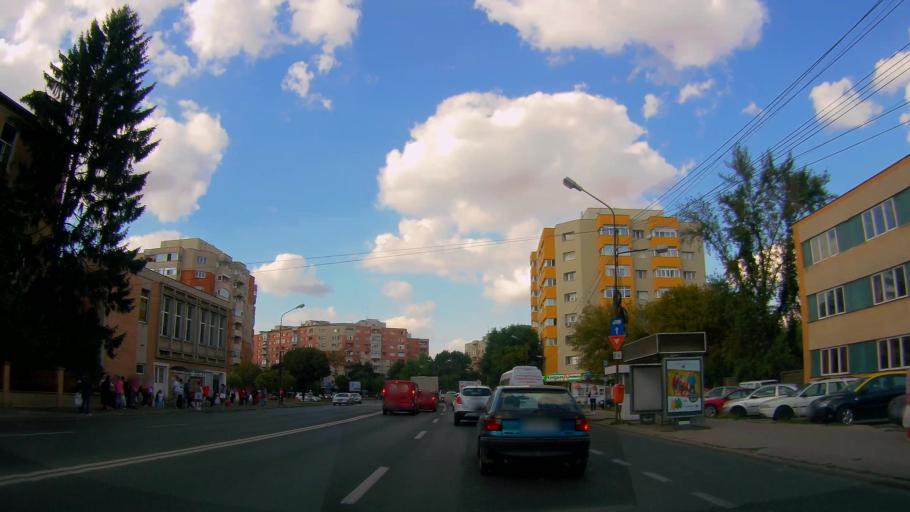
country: RO
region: Satu Mare
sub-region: Municipiul Satu Mare
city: Satu Mare
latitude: 47.7784
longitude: 22.8833
